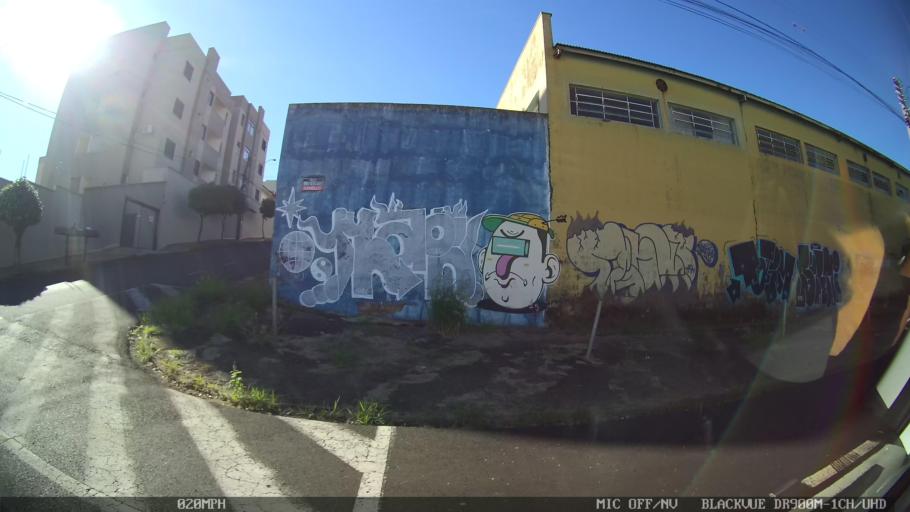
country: BR
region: Sao Paulo
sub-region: Franca
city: Franca
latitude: -20.5481
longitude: -47.4082
